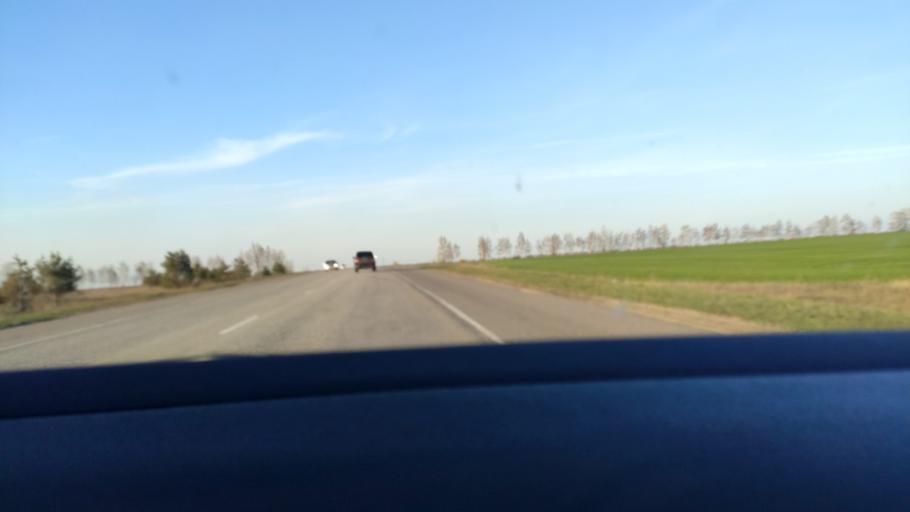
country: RU
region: Voronezj
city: Kolodeznyy
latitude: 51.3908
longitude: 39.2293
